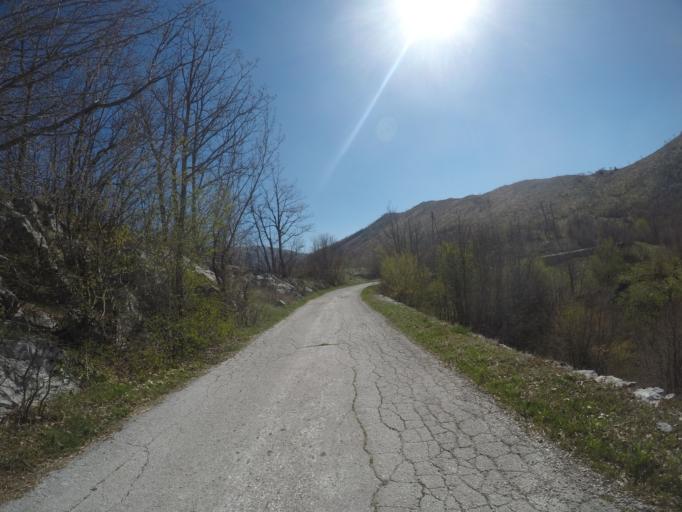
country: ME
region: Danilovgrad
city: Danilovgrad
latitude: 42.5373
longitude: 18.9856
